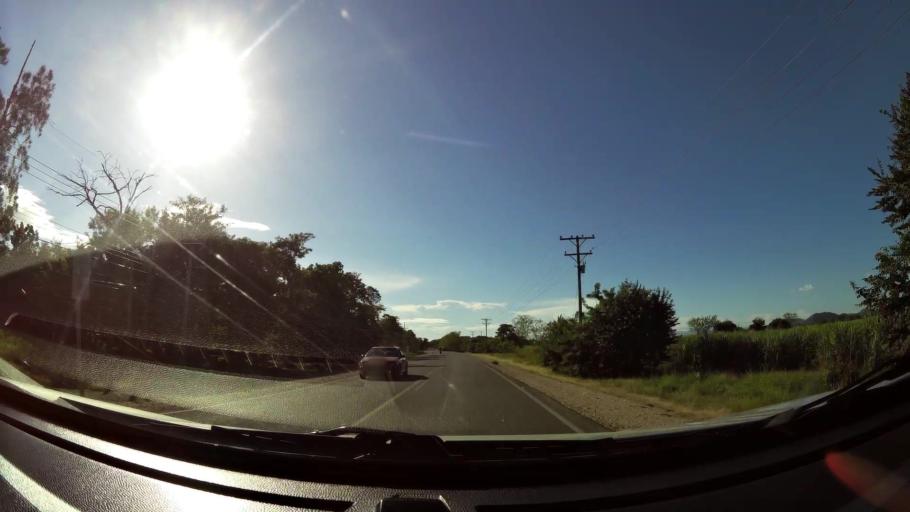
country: CR
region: Guanacaste
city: Belen
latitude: 10.4678
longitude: -85.5612
